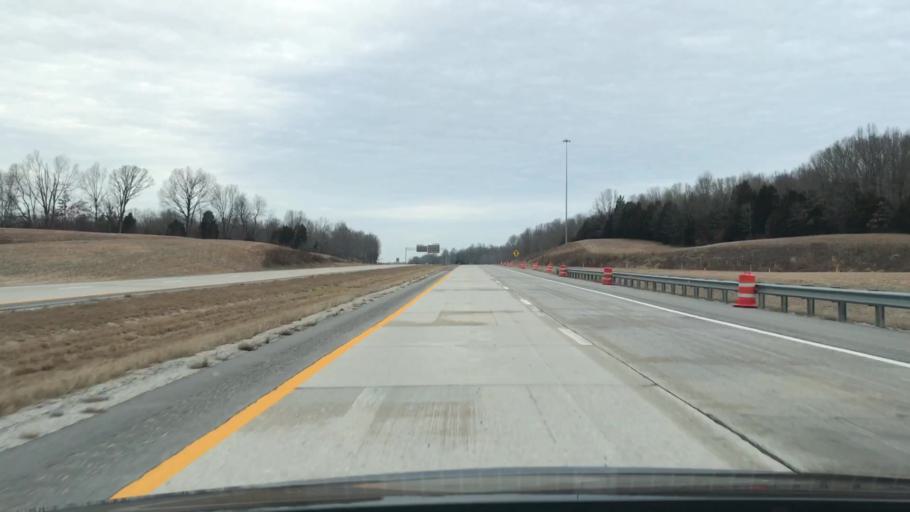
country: US
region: Kentucky
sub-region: Ohio County
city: Beaver Dam
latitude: 37.3862
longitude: -86.8100
